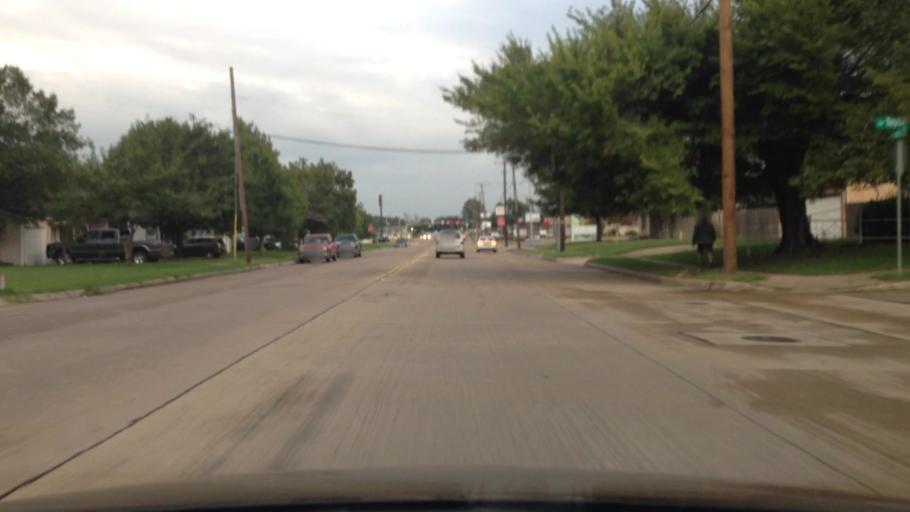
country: US
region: Texas
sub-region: Johnson County
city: Burleson
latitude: 32.5474
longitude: -97.3300
